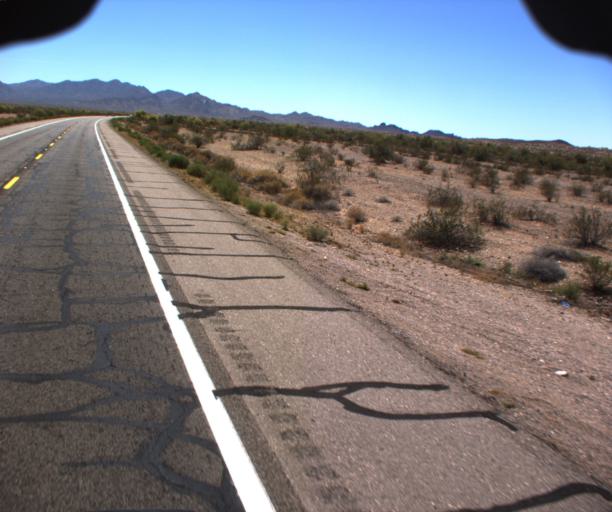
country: US
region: Arizona
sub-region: Mohave County
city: Desert Hills
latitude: 34.7105
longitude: -114.3061
